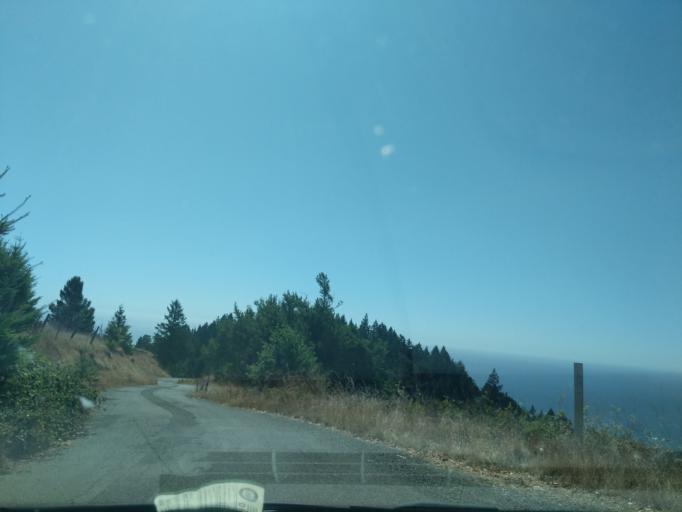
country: US
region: California
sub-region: Sonoma County
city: Monte Rio
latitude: 38.5297
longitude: -123.2259
